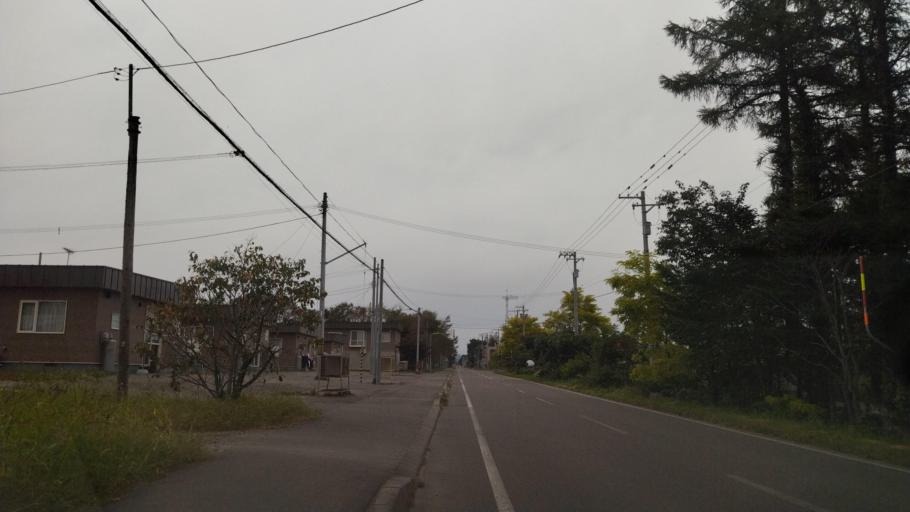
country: JP
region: Hokkaido
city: Otofuke
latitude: 43.2240
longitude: 143.2792
